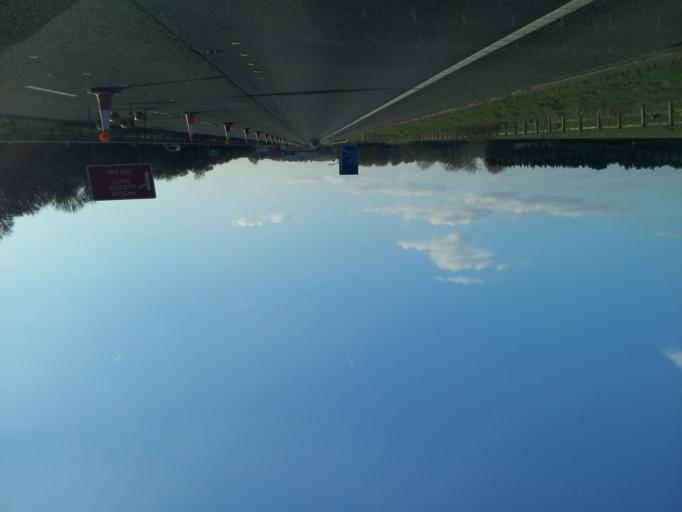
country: GB
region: England
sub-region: Devon
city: Cullompton
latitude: 50.8668
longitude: -3.3828
